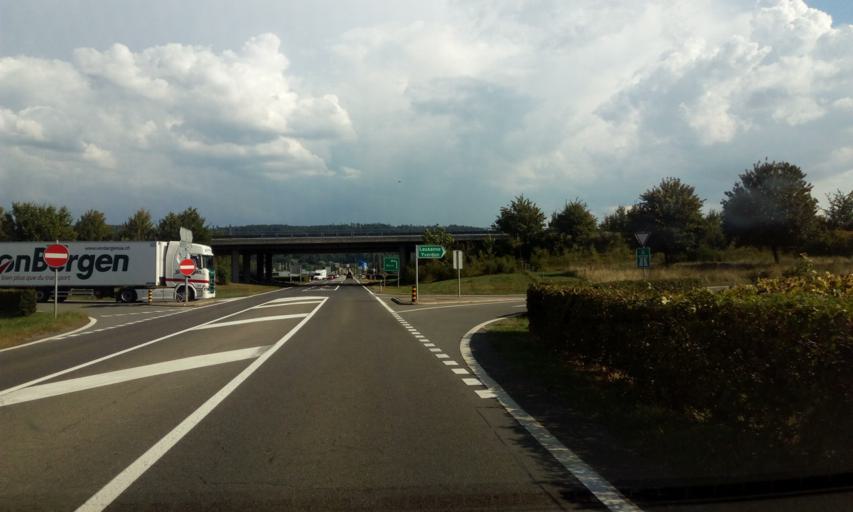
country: CH
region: Vaud
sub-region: Broye-Vully District
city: Avenches
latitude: 46.8829
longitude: 7.0246
